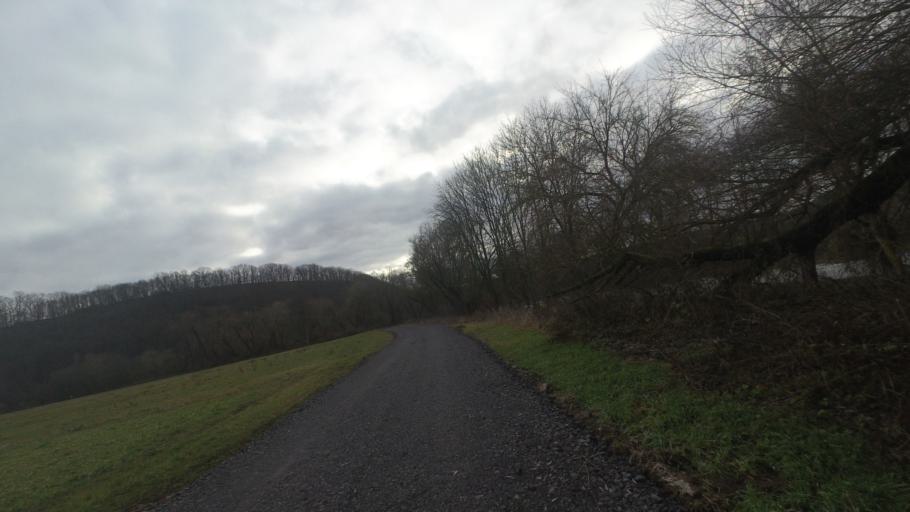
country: DE
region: Thuringia
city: Orlamunde
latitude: 50.7690
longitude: 11.5205
